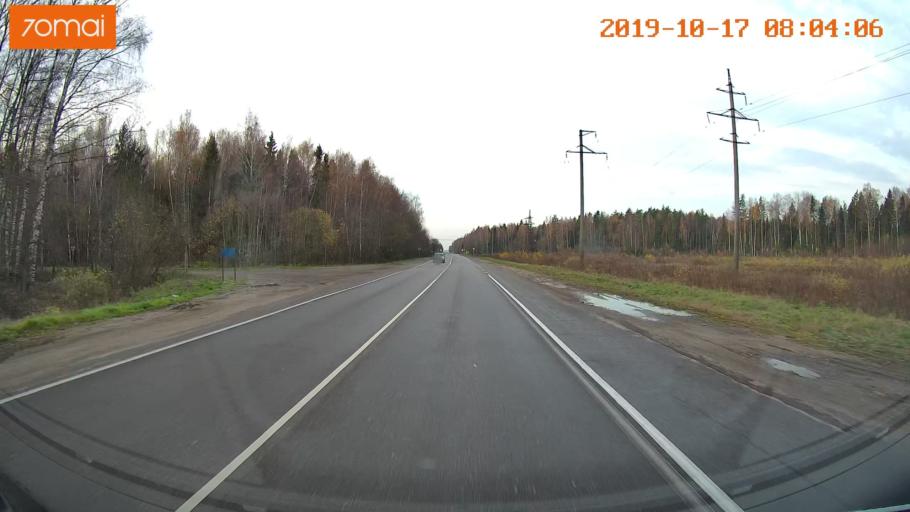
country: RU
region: Vladimir
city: Belaya Rechka
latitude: 56.3489
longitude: 39.4419
